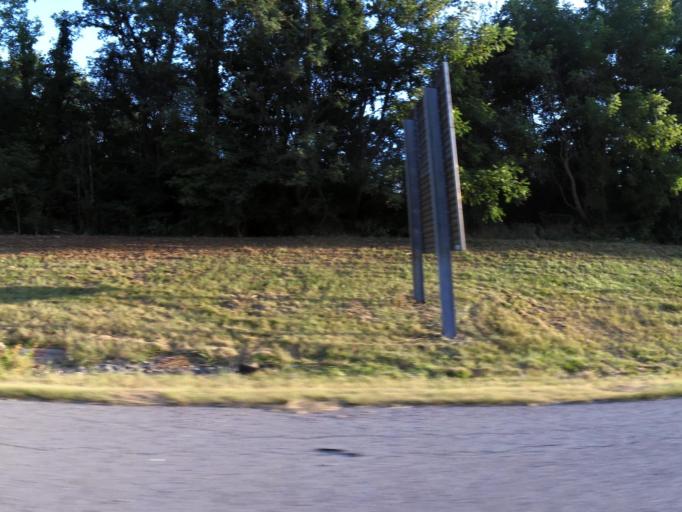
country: US
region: Indiana
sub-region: Boone County
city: Zionsville
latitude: 39.9307
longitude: -86.2835
